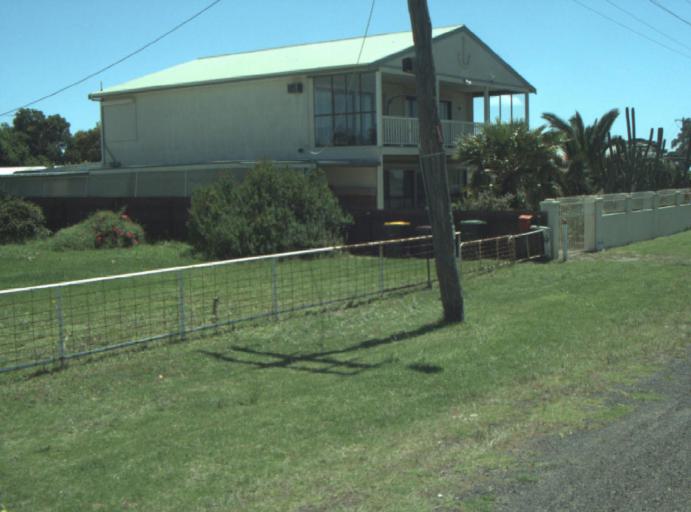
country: AU
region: Victoria
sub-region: Queenscliffe
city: Queenscliff
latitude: -38.1754
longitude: 144.7173
